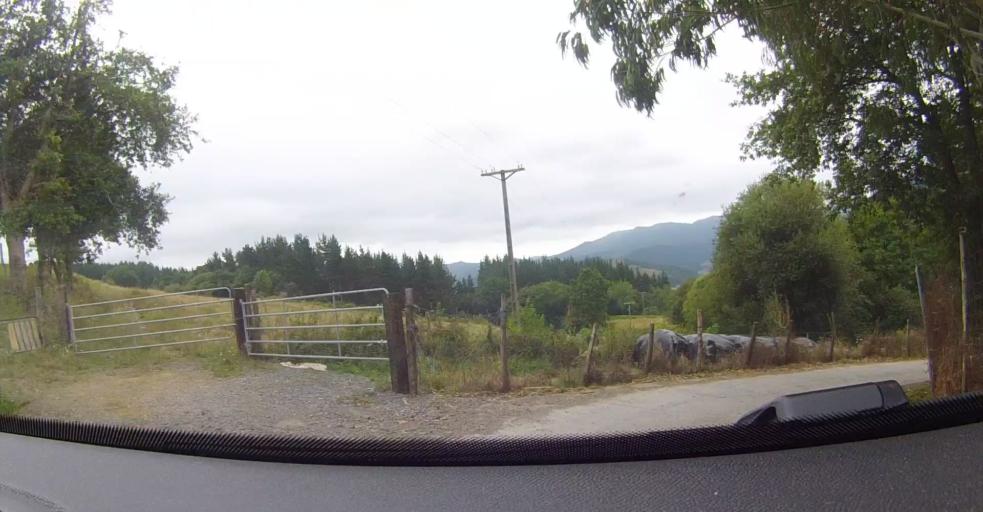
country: ES
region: Basque Country
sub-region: Bizkaia
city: Urrestieta
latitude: 43.2342
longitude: -3.1821
